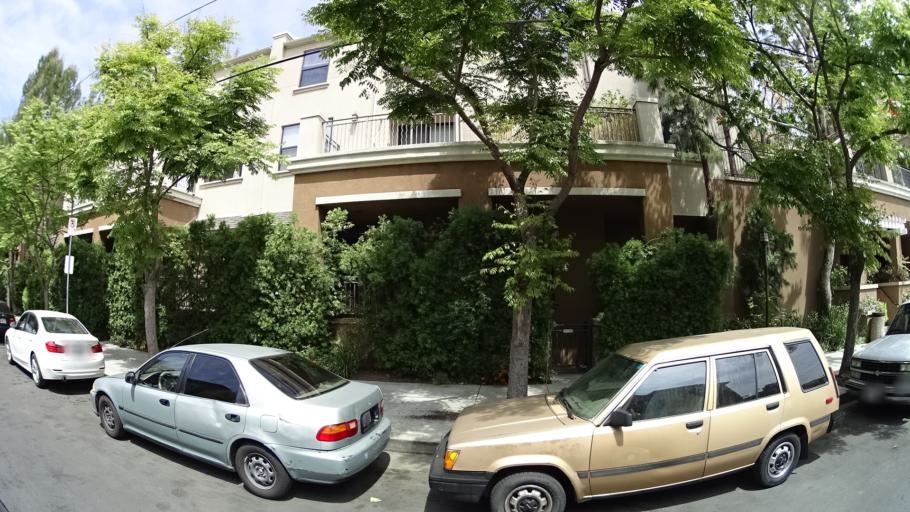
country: US
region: California
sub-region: Los Angeles County
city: Los Angeles
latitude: 34.0562
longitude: -118.2619
